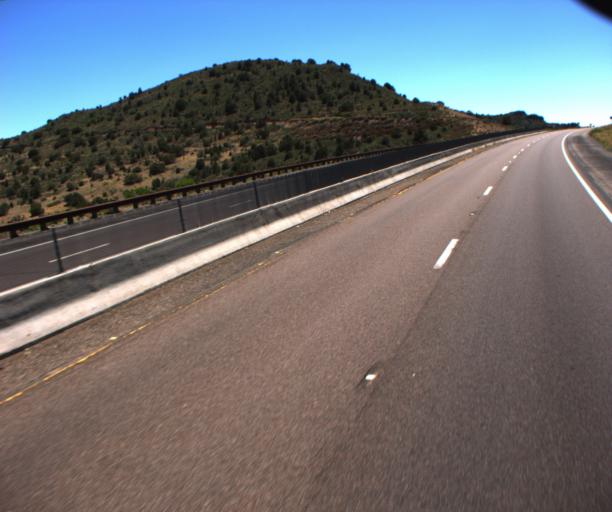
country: US
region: Arizona
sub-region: Gila County
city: Tonto Basin
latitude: 33.9256
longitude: -111.4483
